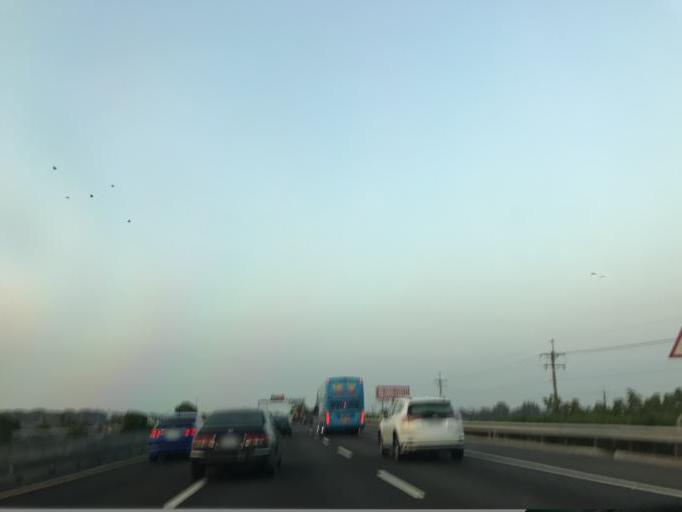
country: TW
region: Taiwan
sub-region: Yunlin
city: Douliu
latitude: 23.7102
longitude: 120.4762
